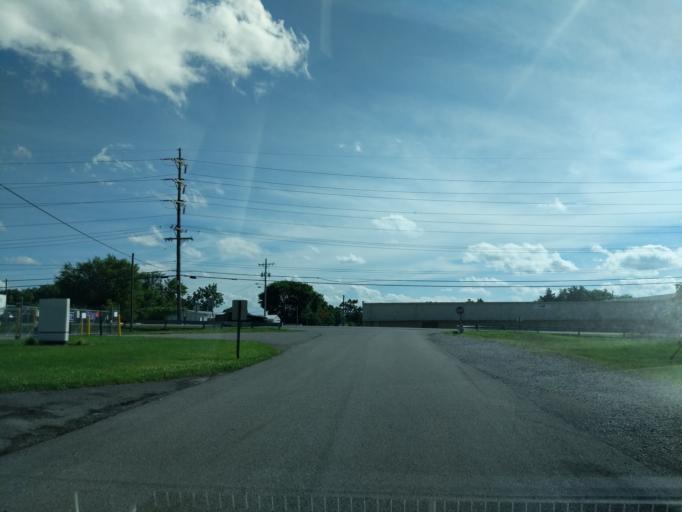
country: US
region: Tennessee
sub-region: Davidson County
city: Lakewood
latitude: 36.2743
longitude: -86.6649
